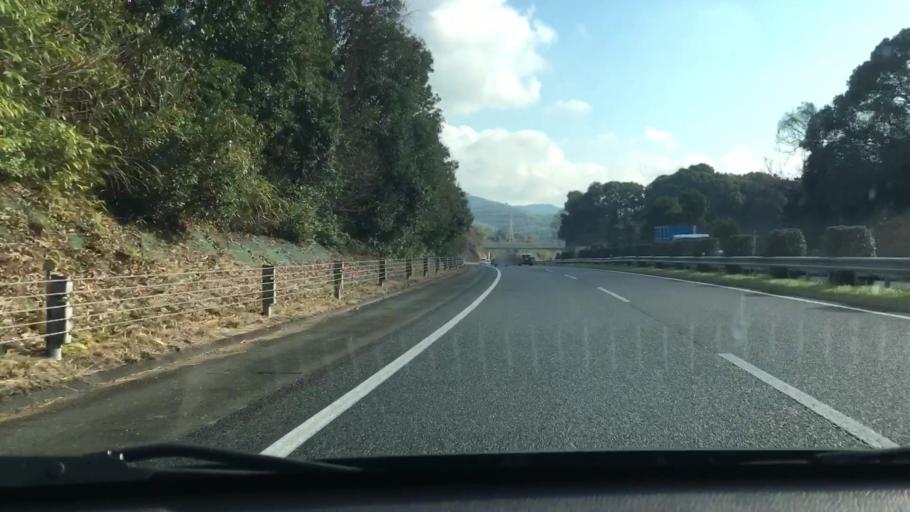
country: JP
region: Kumamoto
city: Matsubase
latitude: 32.6400
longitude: 130.7076
